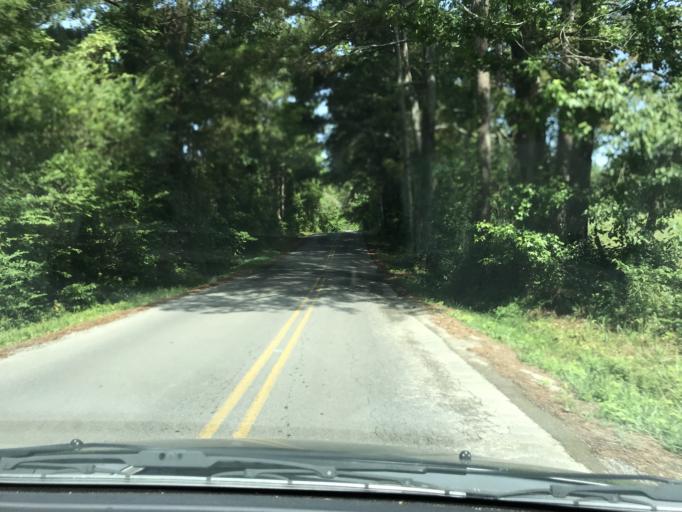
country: US
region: Tennessee
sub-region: Hamilton County
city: Apison
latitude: 35.0501
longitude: -84.9926
